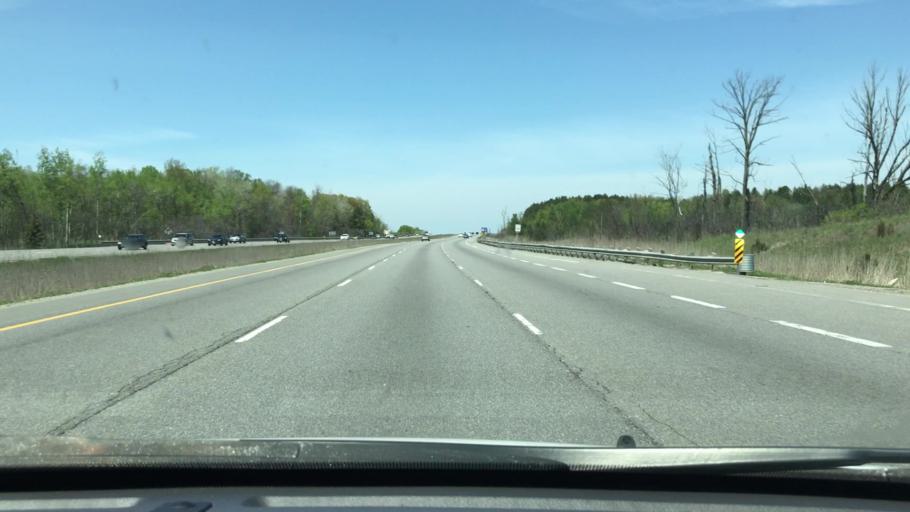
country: CA
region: Ontario
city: Newmarket
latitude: 43.9838
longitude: -79.3941
